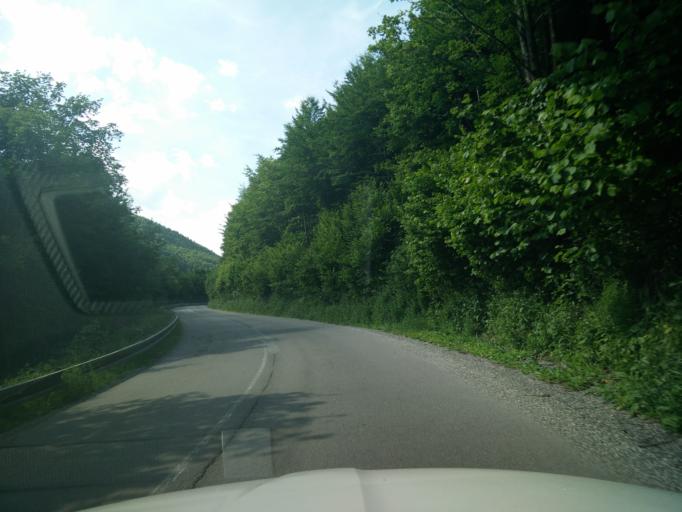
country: SK
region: Zilinsky
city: Rajec
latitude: 48.9594
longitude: 18.6145
